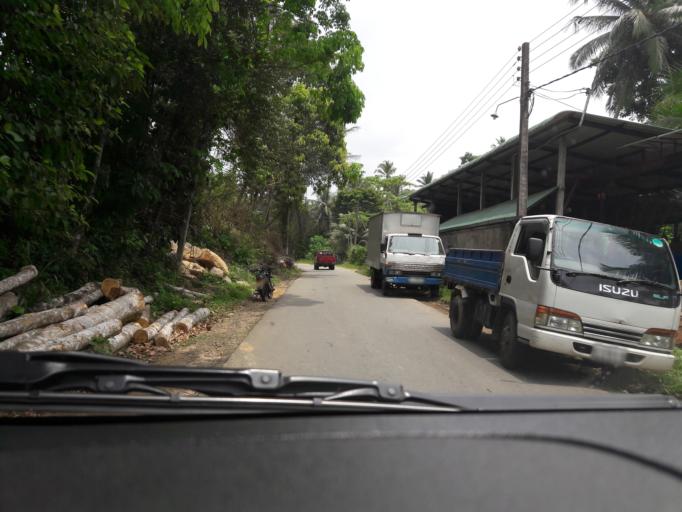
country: LK
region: Southern
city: Galle
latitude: 6.1771
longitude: 80.2890
